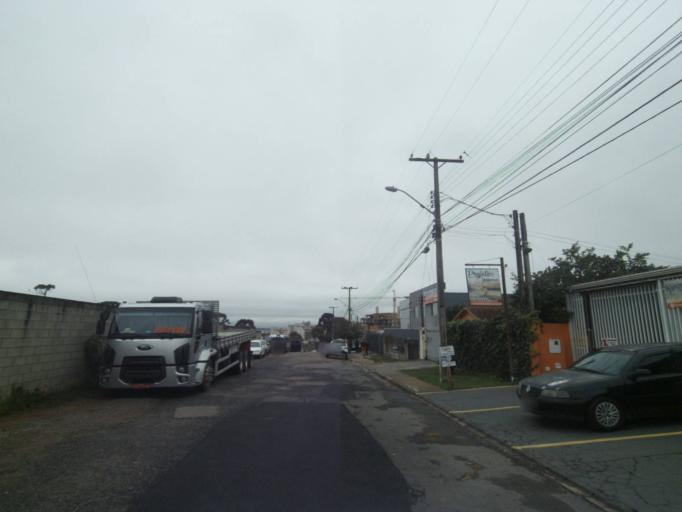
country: BR
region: Parana
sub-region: Curitiba
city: Curitiba
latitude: -25.4988
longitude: -49.3086
